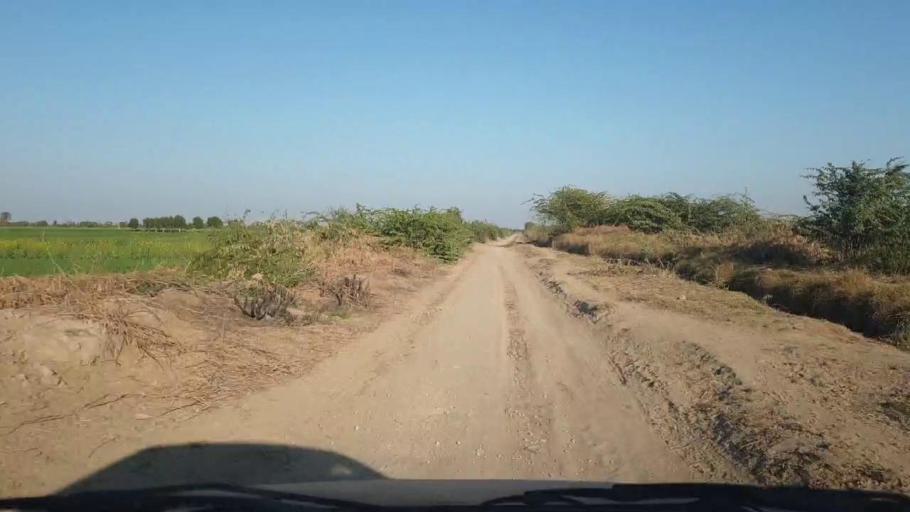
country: PK
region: Sindh
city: Samaro
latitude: 25.3263
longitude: 69.3088
